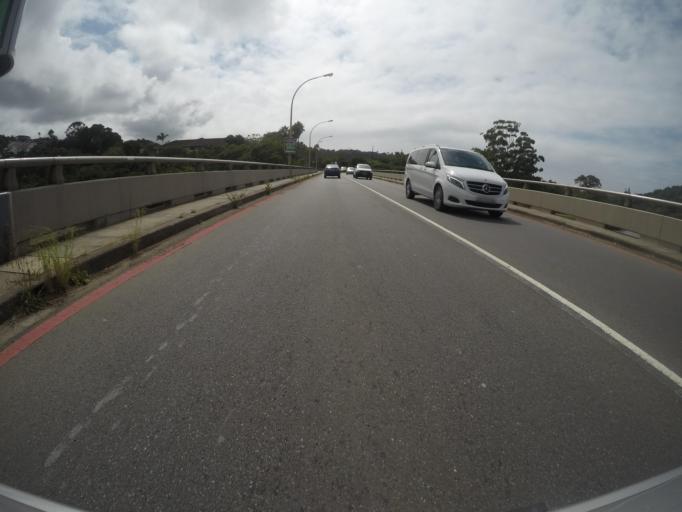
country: ZA
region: Eastern Cape
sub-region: Buffalo City Metropolitan Municipality
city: East London
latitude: -32.9738
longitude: 27.9255
